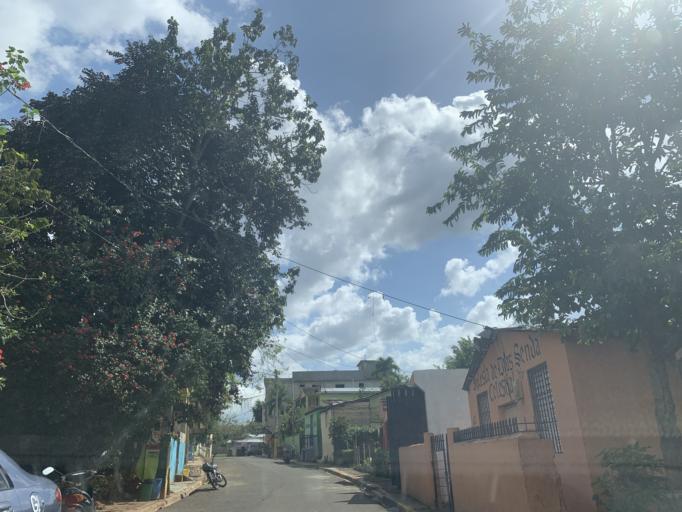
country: DO
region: Monte Plata
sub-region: Yamasa
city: Yamasa
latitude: 18.7747
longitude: -70.0279
